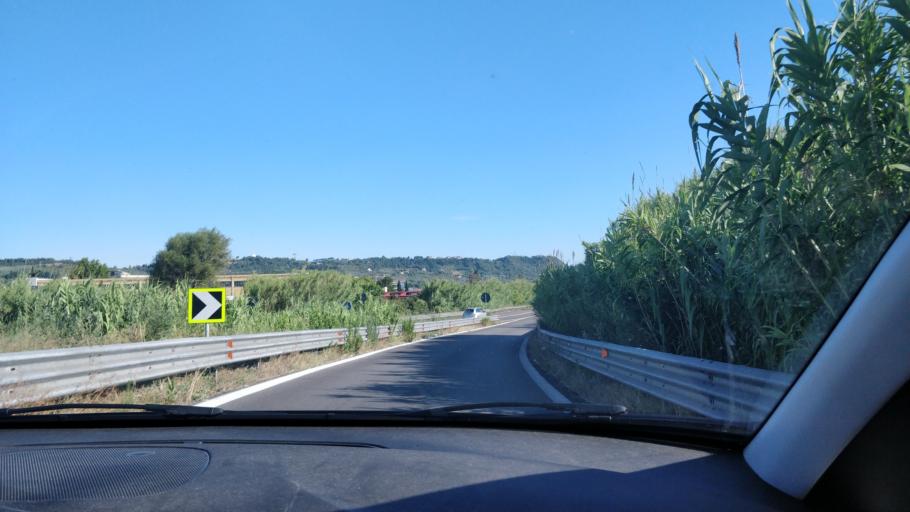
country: IT
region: Abruzzo
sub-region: Provincia di Pescara
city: Villa Raspa
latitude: 42.4423
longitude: 14.1941
